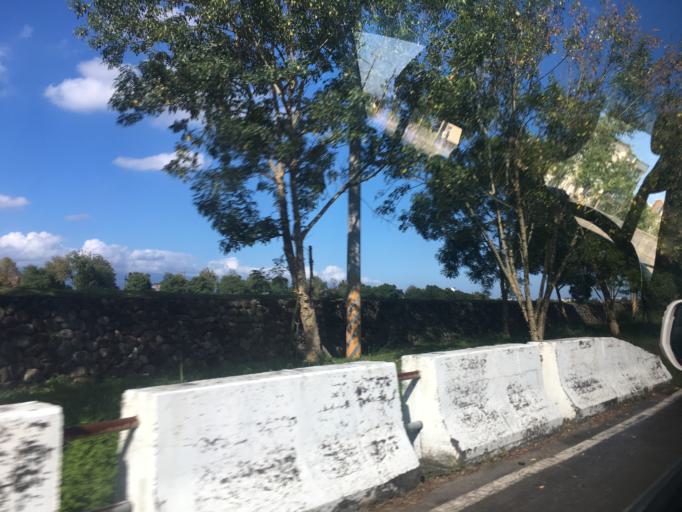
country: TW
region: Taiwan
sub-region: Yilan
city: Yilan
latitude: 24.6924
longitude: 121.7409
